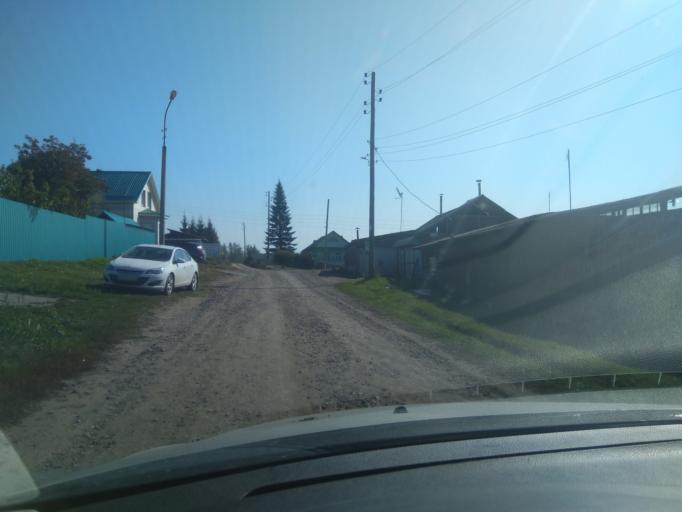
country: RU
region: Sverdlovsk
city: Pokrovskoye
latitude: 56.4369
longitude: 61.5999
